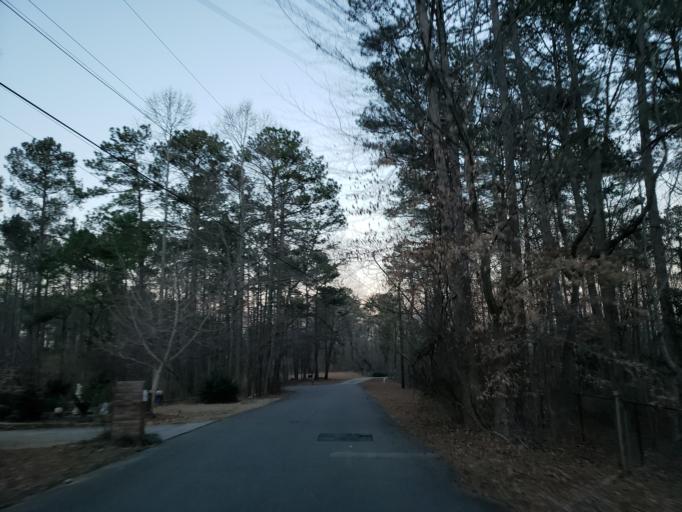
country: US
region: Georgia
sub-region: Cobb County
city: Mableton
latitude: 33.8505
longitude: -84.5645
